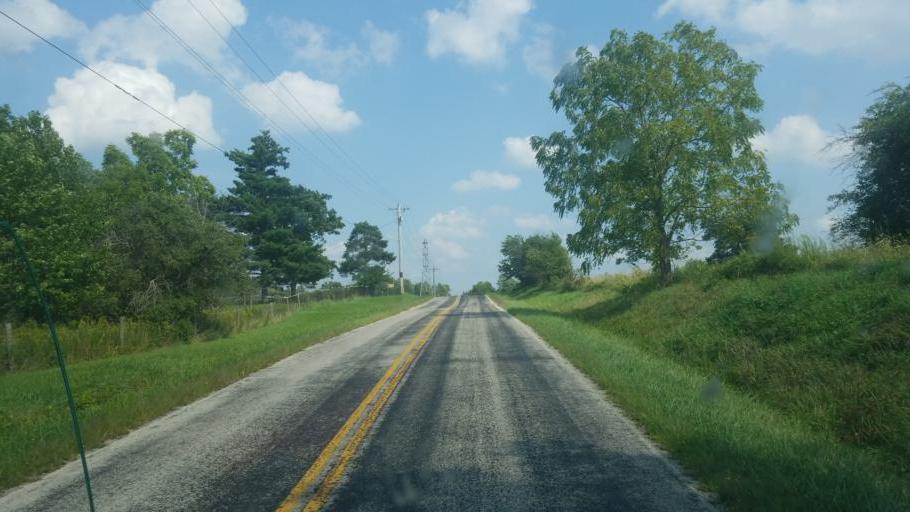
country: US
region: Ohio
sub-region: Lorain County
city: Wellington
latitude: 41.0576
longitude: -82.2756
